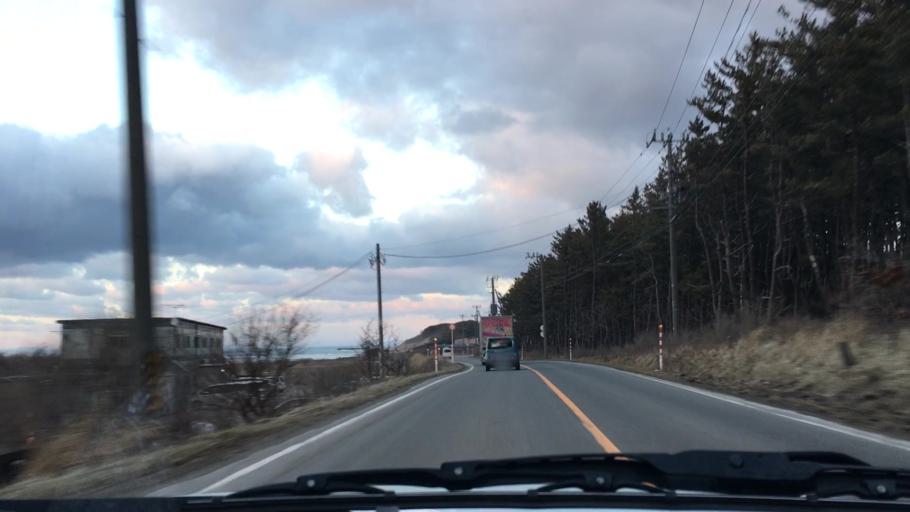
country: JP
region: Aomori
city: Shimokizukuri
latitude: 40.7523
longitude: 140.1469
